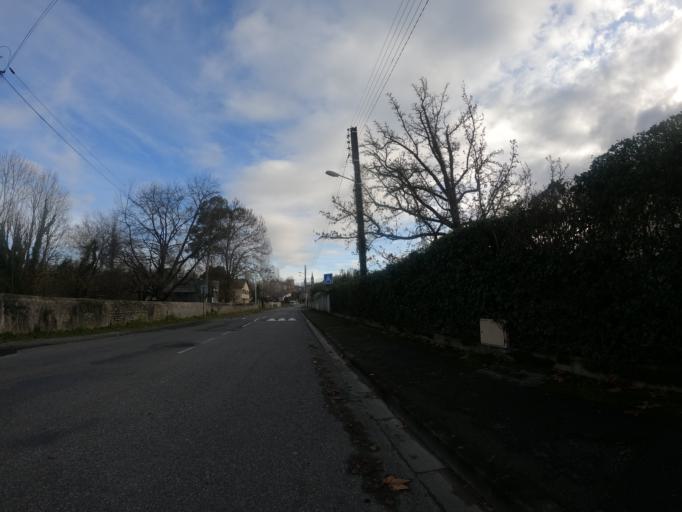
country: FR
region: Aquitaine
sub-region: Departement des Pyrenees-Atlantiques
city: Jurancon
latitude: 43.2930
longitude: -0.3847
